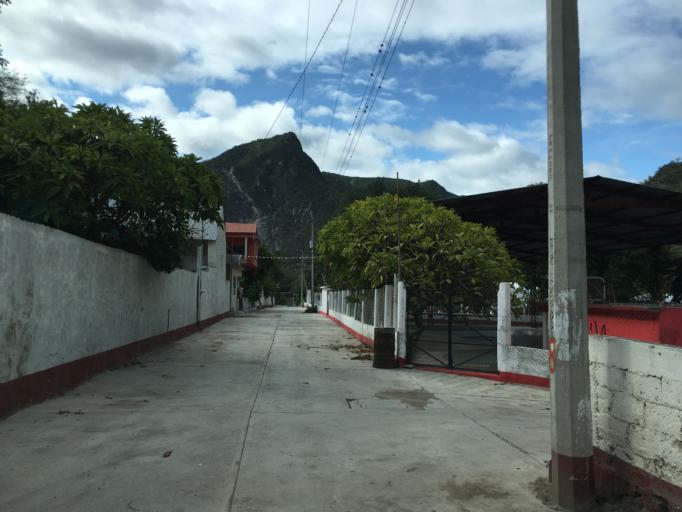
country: MX
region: Hidalgo
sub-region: Metztitlan
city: Fontezuelas
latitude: 20.6397
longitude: -98.9205
